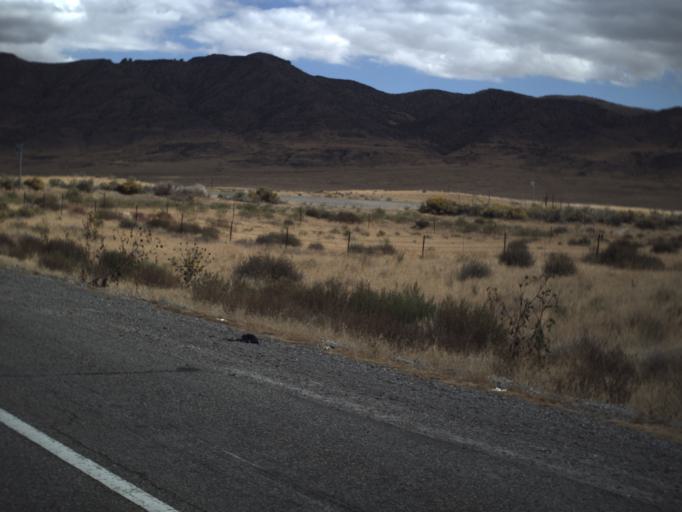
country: US
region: Utah
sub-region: Tooele County
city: Grantsville
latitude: 40.7674
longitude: -112.9849
